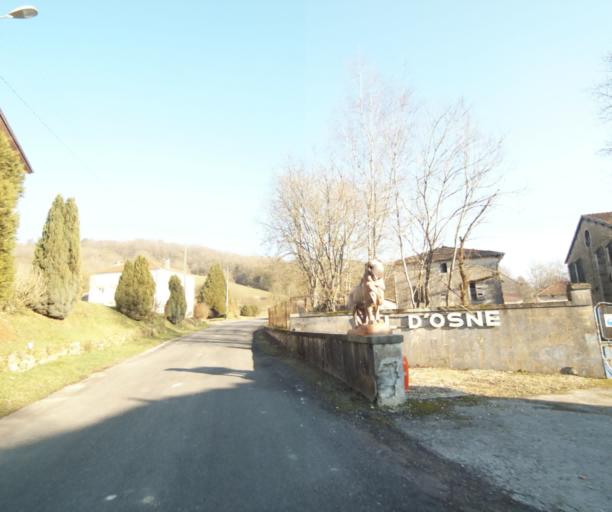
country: FR
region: Champagne-Ardenne
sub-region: Departement de la Haute-Marne
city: Chevillon
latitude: 48.5039
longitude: 5.1728
